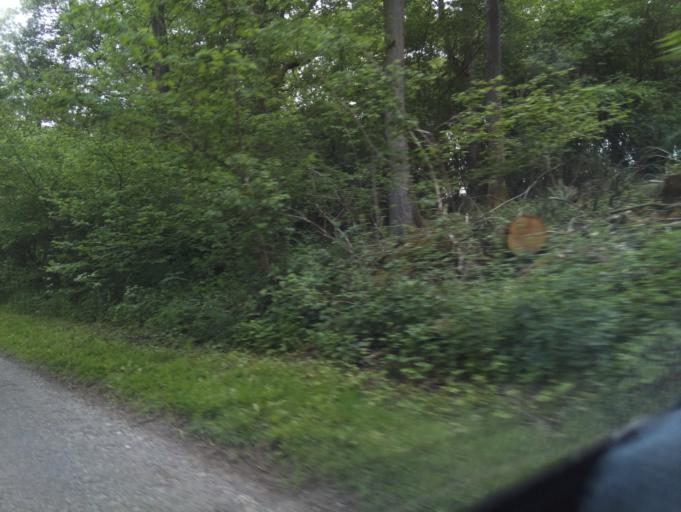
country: GB
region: England
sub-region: Herefordshire
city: Yatton
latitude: 51.9586
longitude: -2.5256
